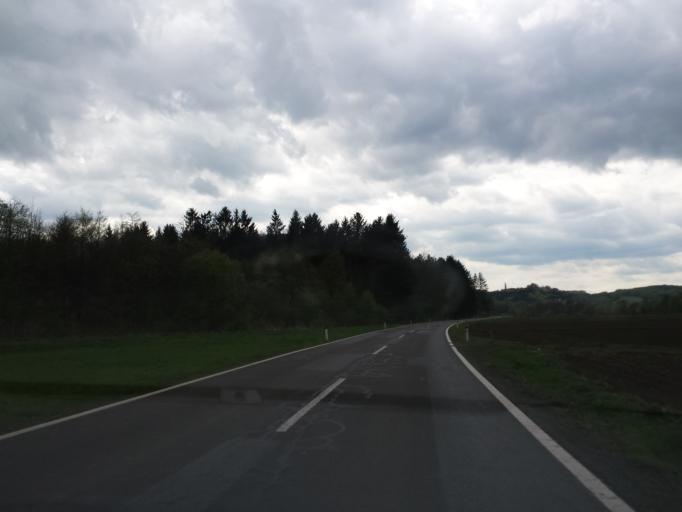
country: AT
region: Styria
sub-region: Politischer Bezirk Suedoststeiermark
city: Riegersburg
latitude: 46.9934
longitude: 15.9618
